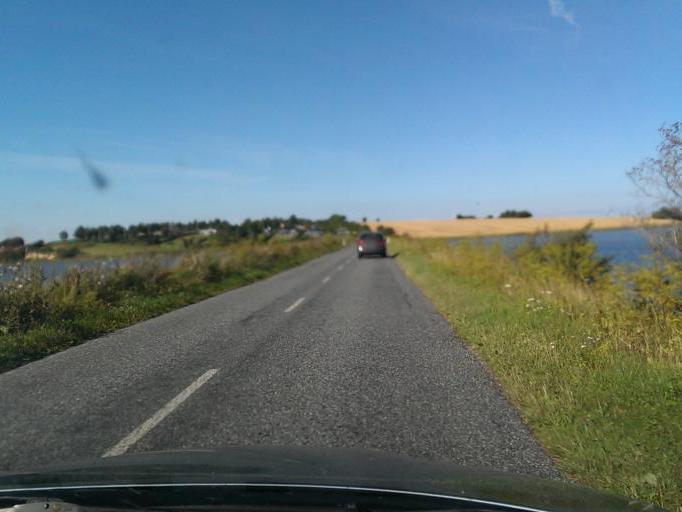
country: DK
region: Central Jutland
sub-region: Odder Kommune
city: Odder
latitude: 55.8676
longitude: 10.1173
